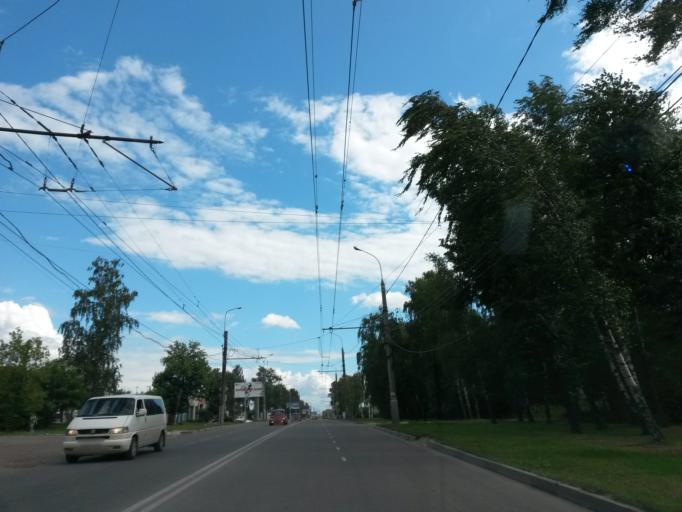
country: RU
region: Ivanovo
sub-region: Gorod Ivanovo
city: Ivanovo
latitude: 56.9824
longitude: 40.9957
